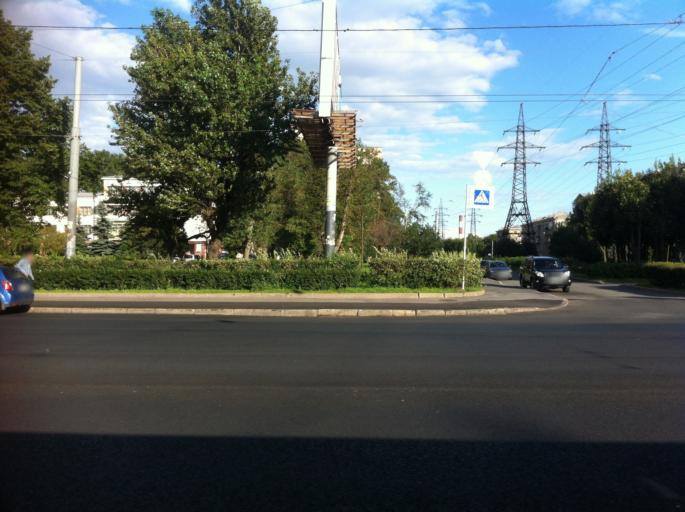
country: RU
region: St.-Petersburg
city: Avtovo
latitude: 59.8779
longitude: 30.2590
